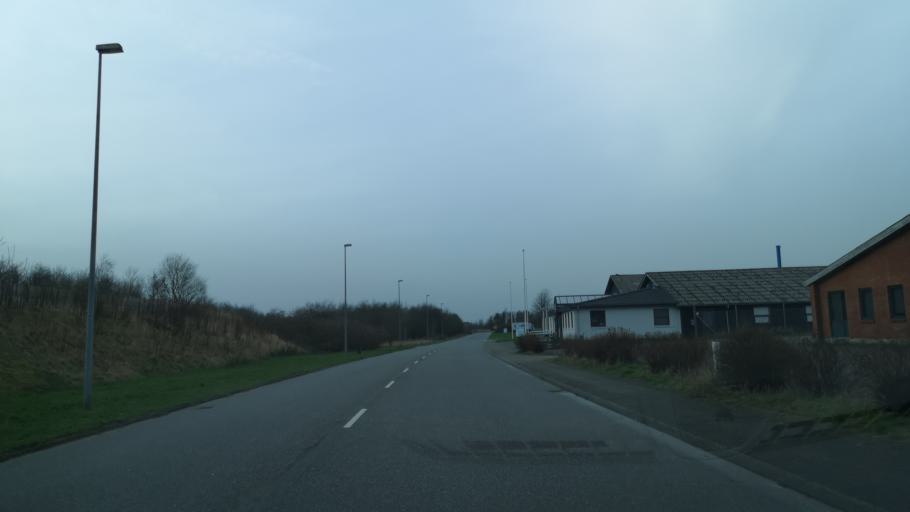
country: DK
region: Central Jutland
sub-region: Herning Kommune
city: Lind
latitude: 56.1117
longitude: 8.9699
